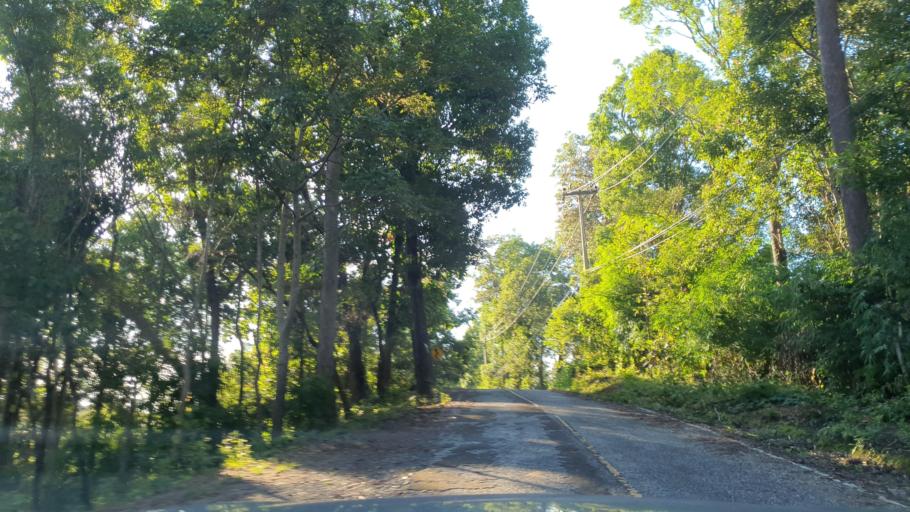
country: TH
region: Chiang Mai
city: Mae On
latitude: 18.8130
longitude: 99.3256
